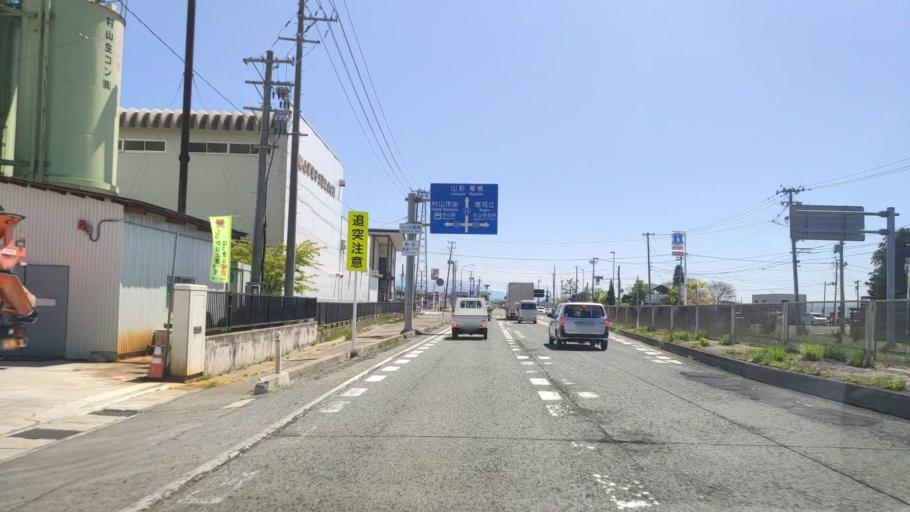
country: JP
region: Yamagata
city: Higashine
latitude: 38.4834
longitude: 140.3830
